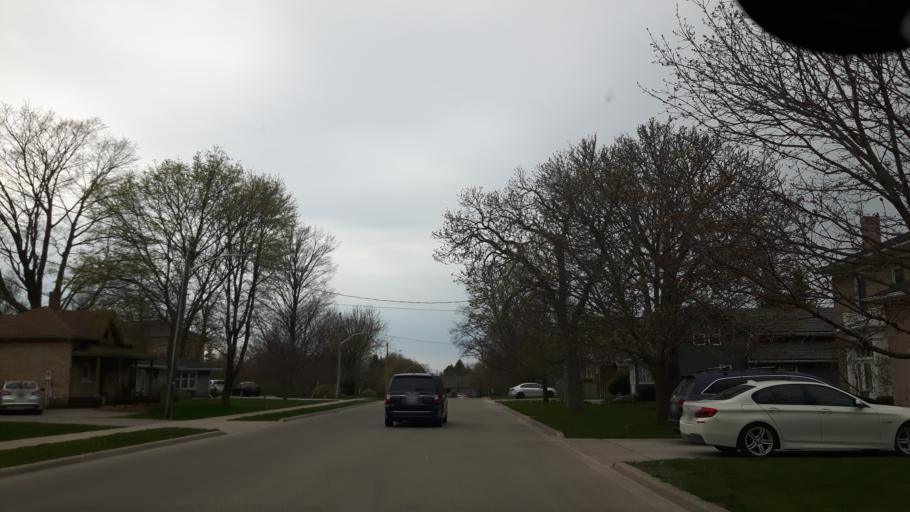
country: CA
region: Ontario
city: Goderich
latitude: 43.7480
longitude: -81.7122
